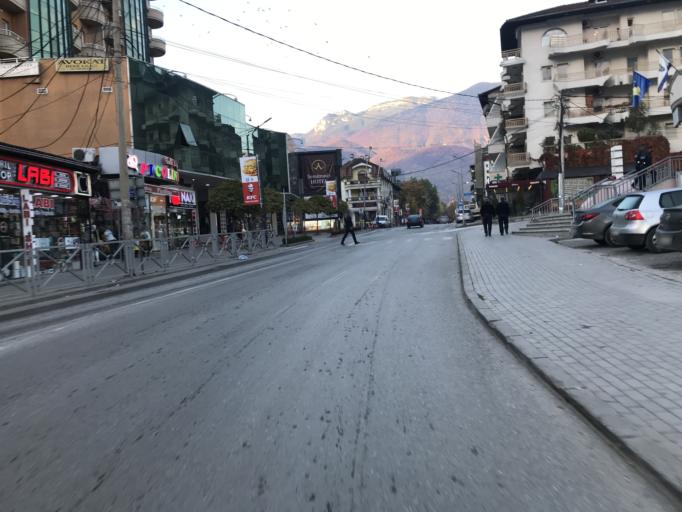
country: XK
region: Pec
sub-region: Komuna e Pejes
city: Peje
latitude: 42.6623
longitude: 20.2965
